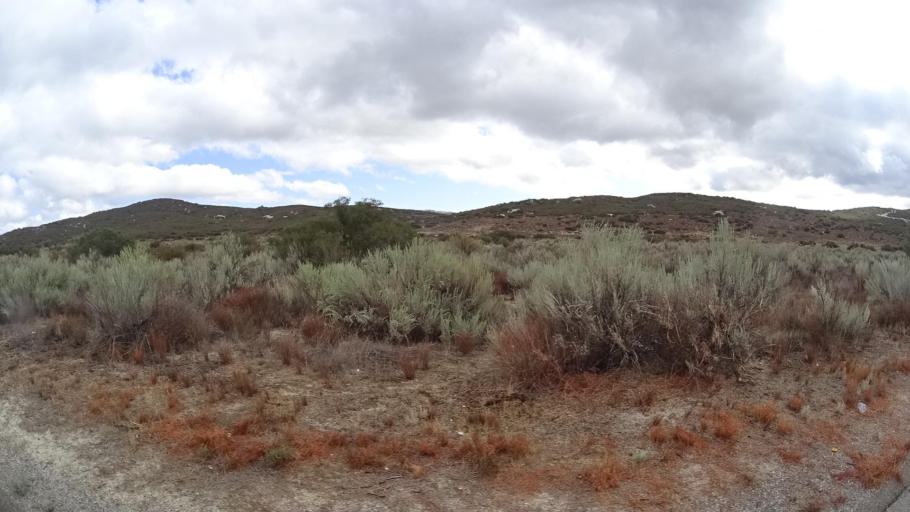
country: US
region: California
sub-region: San Diego County
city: Campo
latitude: 32.6633
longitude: -116.4277
